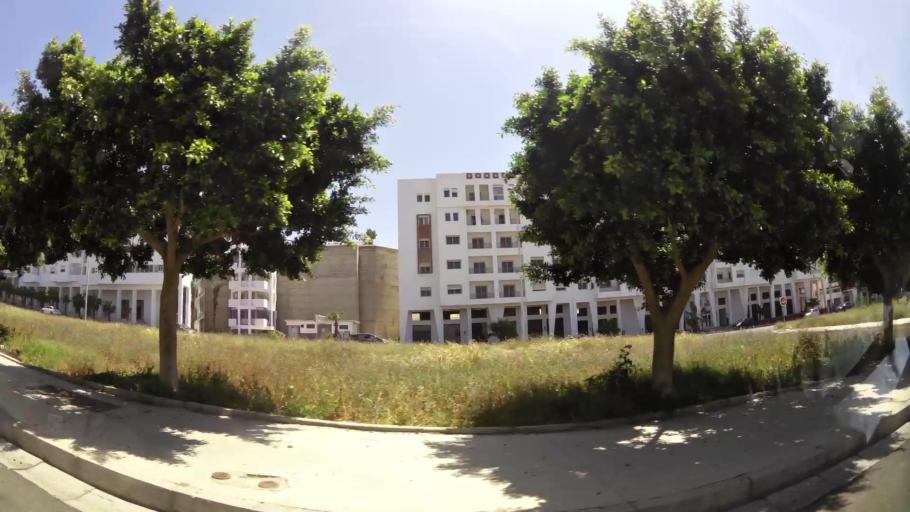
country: MA
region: Souss-Massa-Draa
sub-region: Agadir-Ida-ou-Tnan
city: Agadir
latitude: 30.4342
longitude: -9.5818
